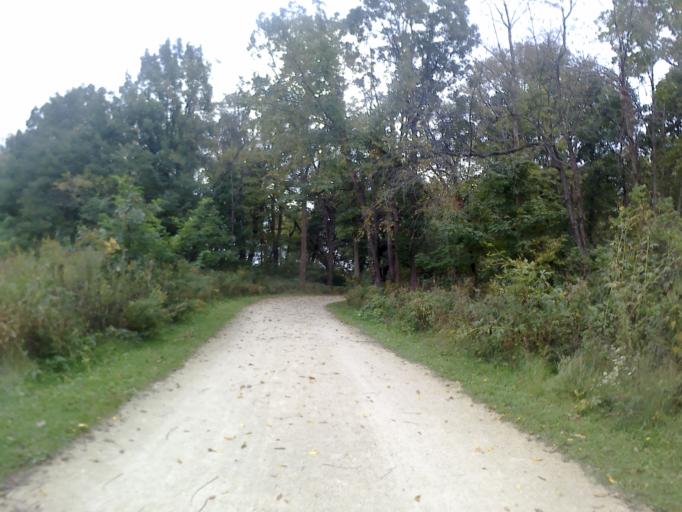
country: US
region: Illinois
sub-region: DuPage County
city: Warrenville
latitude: 41.7930
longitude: -88.1824
